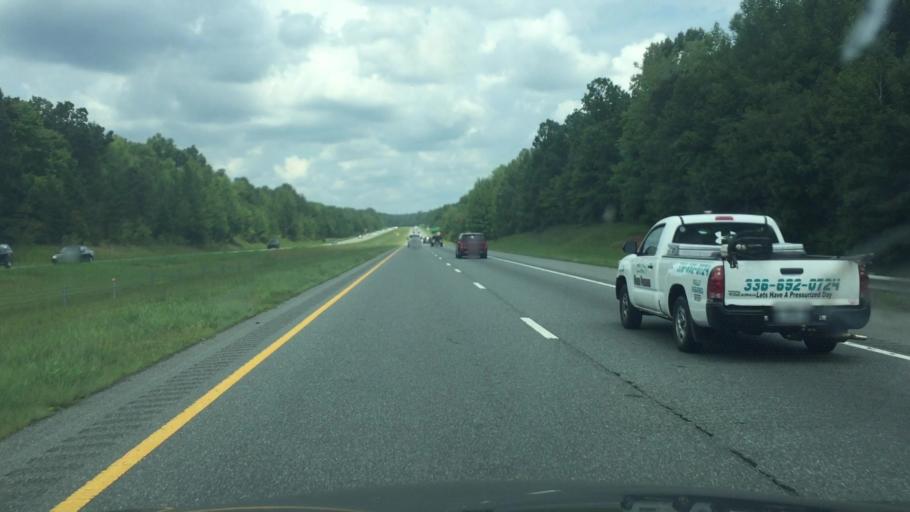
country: US
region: North Carolina
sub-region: Randolph County
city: Asheboro
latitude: 35.5699
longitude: -79.8052
